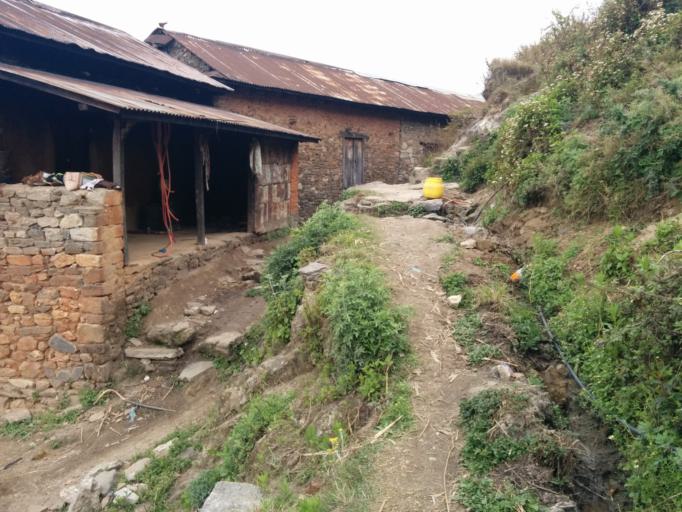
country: NP
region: Central Region
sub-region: Bagmati Zone
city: Bhaktapur
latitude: 27.7785
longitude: 85.4310
